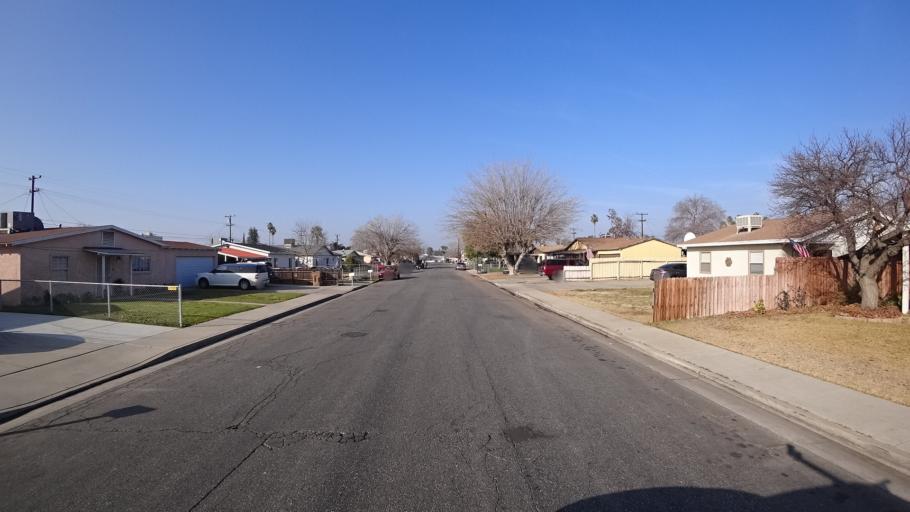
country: US
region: California
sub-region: Kern County
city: Bakersfield
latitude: 35.3348
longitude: -119.0313
